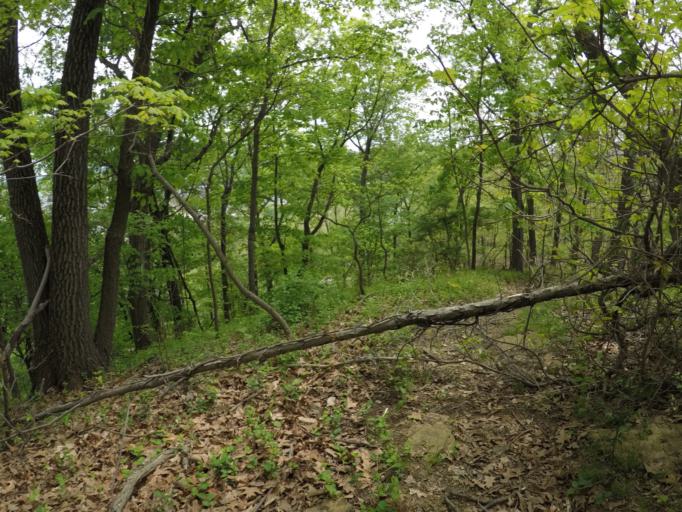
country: US
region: West Virginia
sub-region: Cabell County
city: Huntington
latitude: 38.4166
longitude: -82.3919
